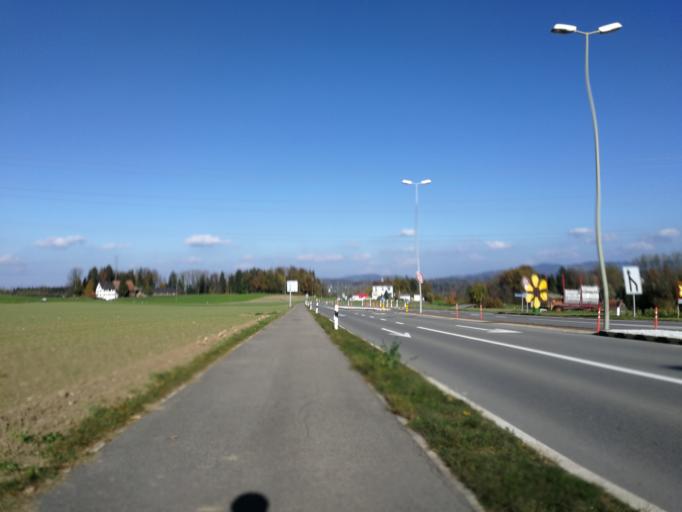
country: CH
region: Zurich
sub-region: Bezirk Uster
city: Esslingen
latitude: 47.2936
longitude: 8.7154
